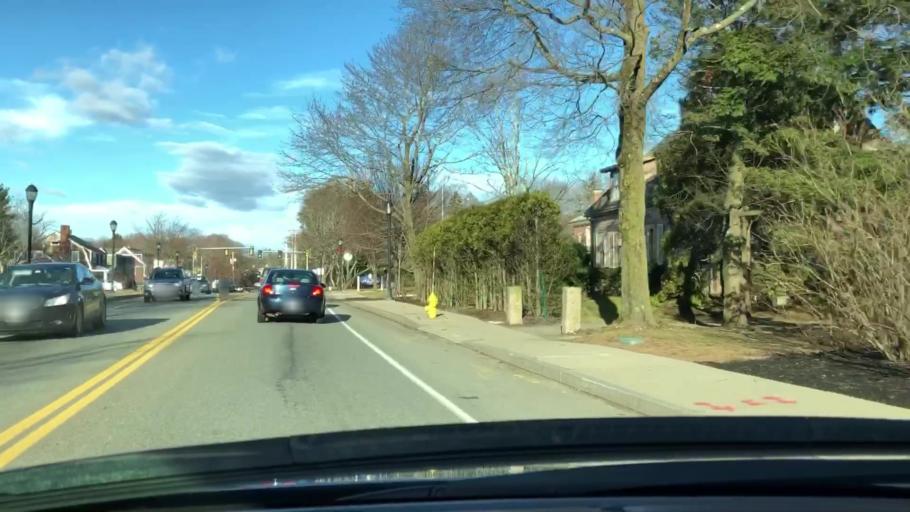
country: US
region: Massachusetts
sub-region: Norfolk County
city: Westwood
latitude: 42.2277
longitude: -71.2217
